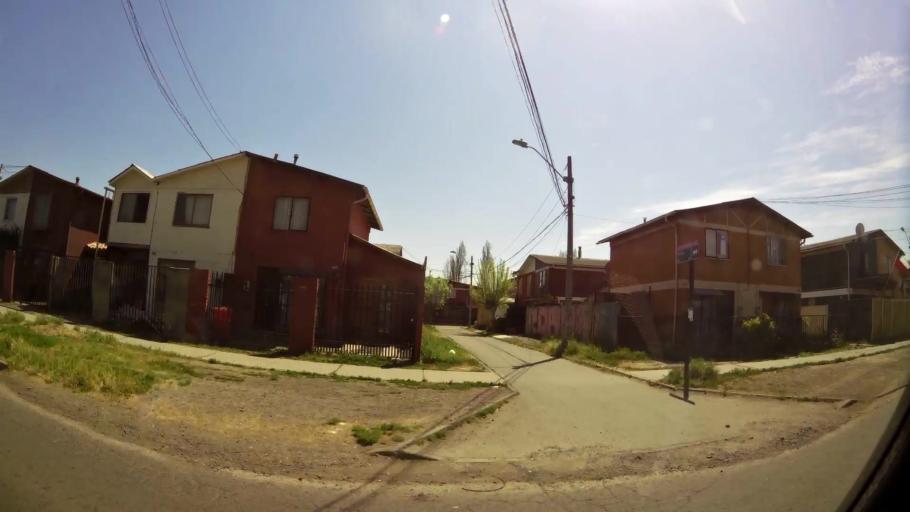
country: CL
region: Santiago Metropolitan
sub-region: Provincia de Talagante
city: Talagante
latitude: -33.6543
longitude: -70.9114
